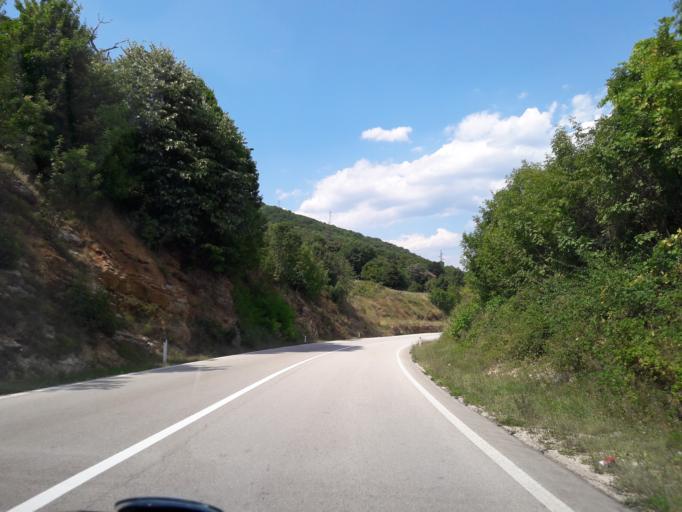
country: BA
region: Republika Srpska
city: Mrkonjic Grad
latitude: 44.5159
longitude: 17.1505
